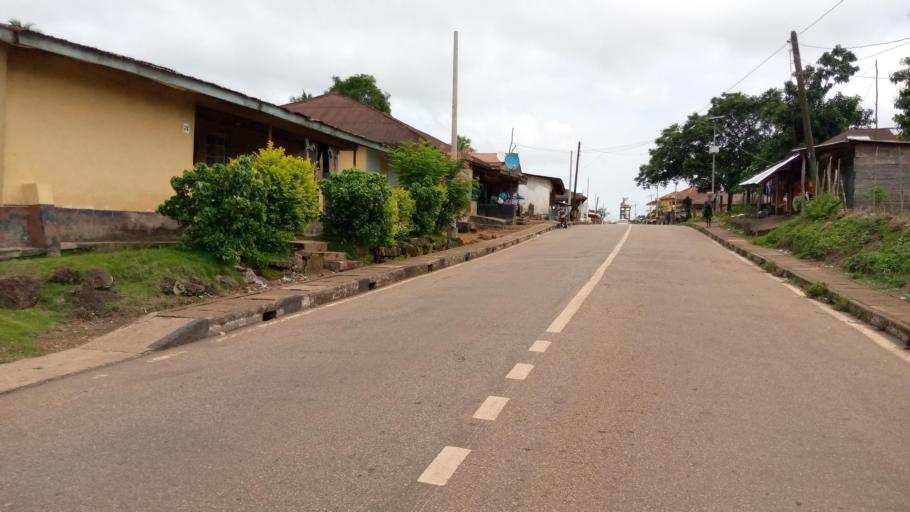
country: SL
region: Southern Province
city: Moyamba
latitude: 8.1583
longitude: -12.4314
